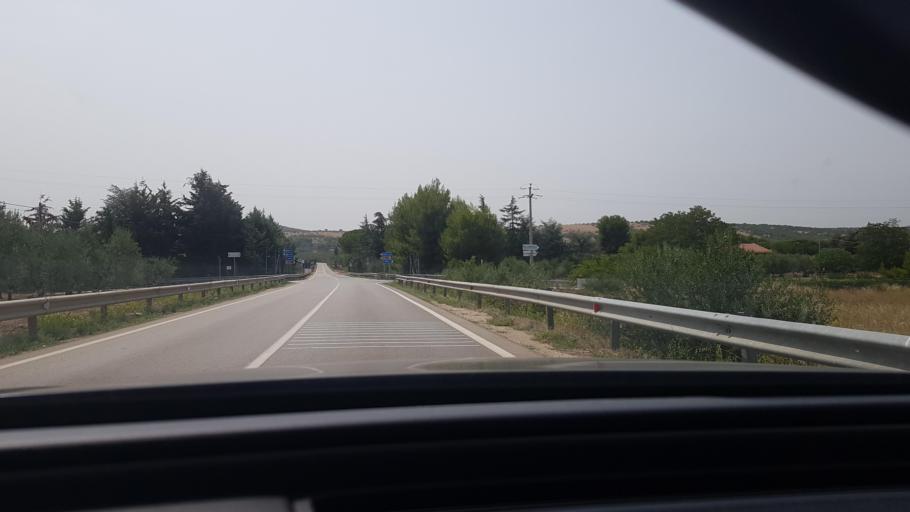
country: IT
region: Apulia
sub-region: Provincia di Barletta - Andria - Trani
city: Andria
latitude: 41.1181
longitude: 16.2836
